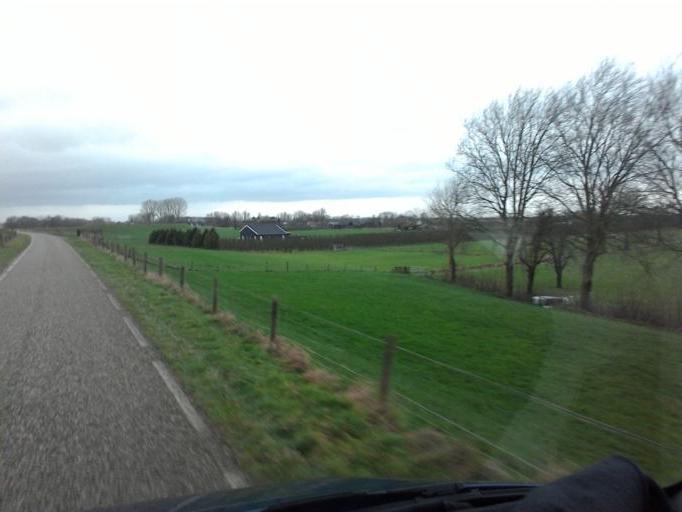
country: NL
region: Utrecht
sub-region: Gemeente Wijk bij Duurstede
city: Wijk bij Duurstede
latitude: 51.9628
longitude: 5.3077
